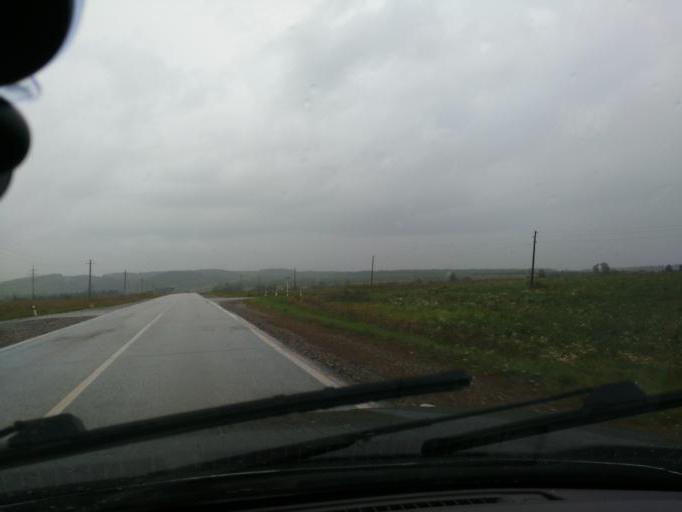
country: RU
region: Perm
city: Barda
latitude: 57.1009
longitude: 55.5291
